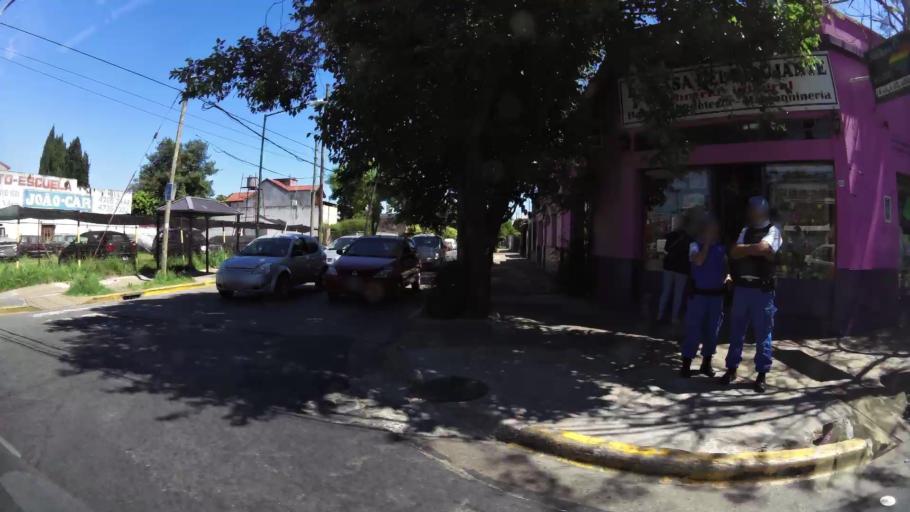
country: AR
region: Buenos Aires
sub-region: Partido de General San Martin
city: General San Martin
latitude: -34.5253
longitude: -58.5482
